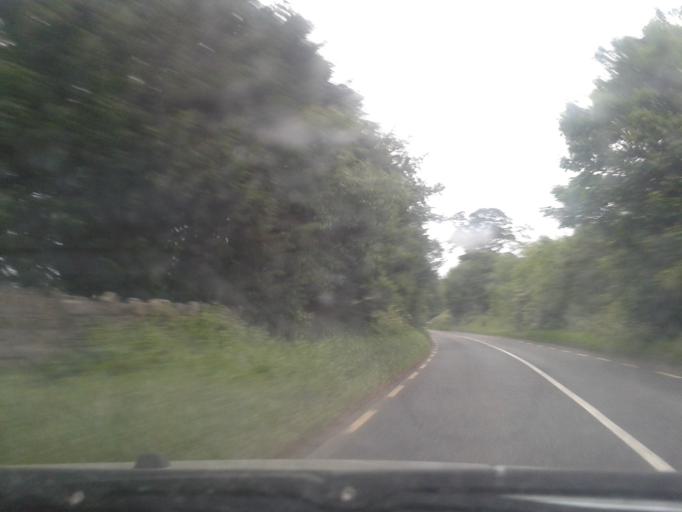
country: IE
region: Leinster
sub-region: Dublin City
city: Finglas
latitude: 53.4142
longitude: -6.3069
